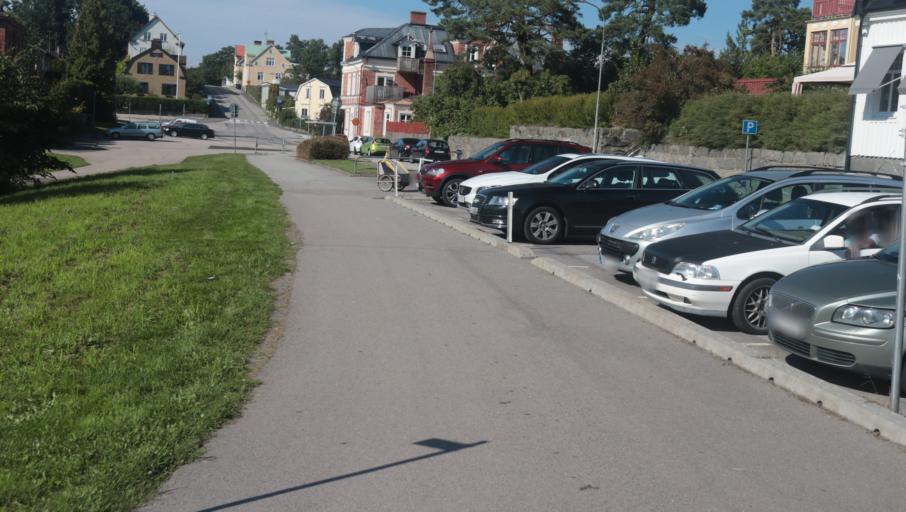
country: SE
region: Blekinge
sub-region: Karlshamns Kommun
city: Karlshamn
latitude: 56.1698
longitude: 14.8546
